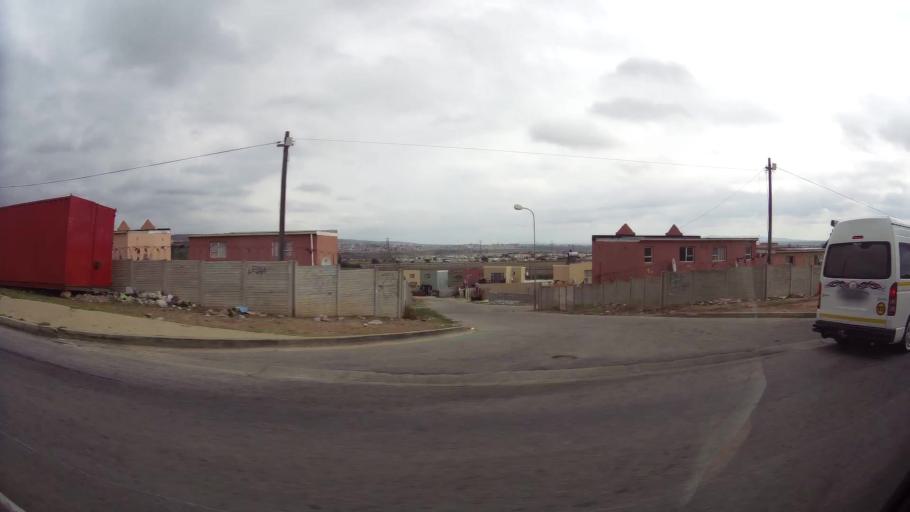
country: ZA
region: Eastern Cape
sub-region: Nelson Mandela Bay Metropolitan Municipality
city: Port Elizabeth
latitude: -33.8911
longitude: 25.5566
